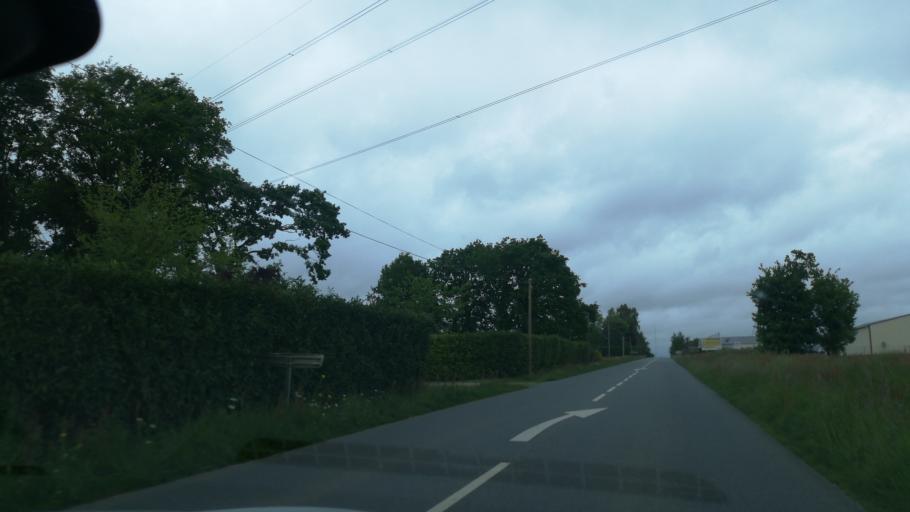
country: FR
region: Brittany
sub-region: Departement d'Ille-et-Vilaine
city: Irodouer
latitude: 48.2402
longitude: -1.9481
